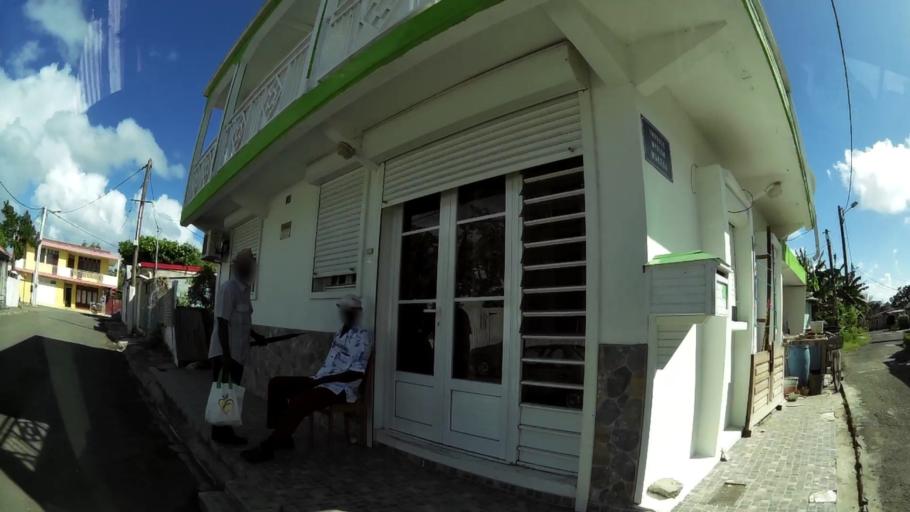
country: GP
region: Guadeloupe
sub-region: Guadeloupe
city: Port-Louis
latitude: 16.4162
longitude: -61.5321
